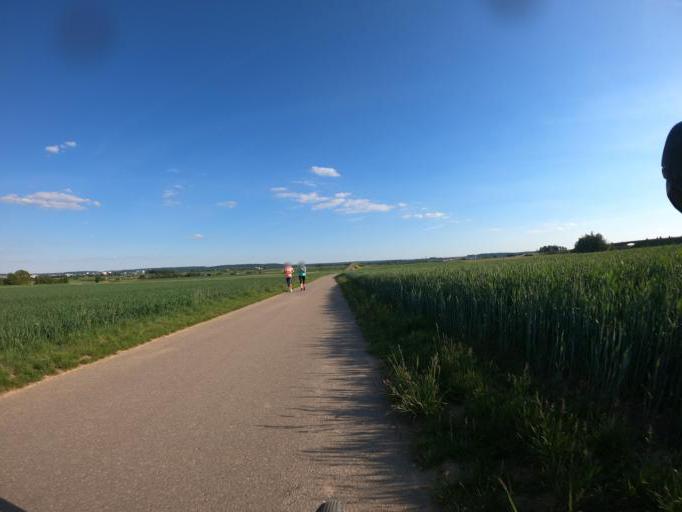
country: DE
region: Baden-Wuerttemberg
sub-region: Regierungsbezirk Stuttgart
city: Magstadt
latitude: 48.7125
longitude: 8.9560
